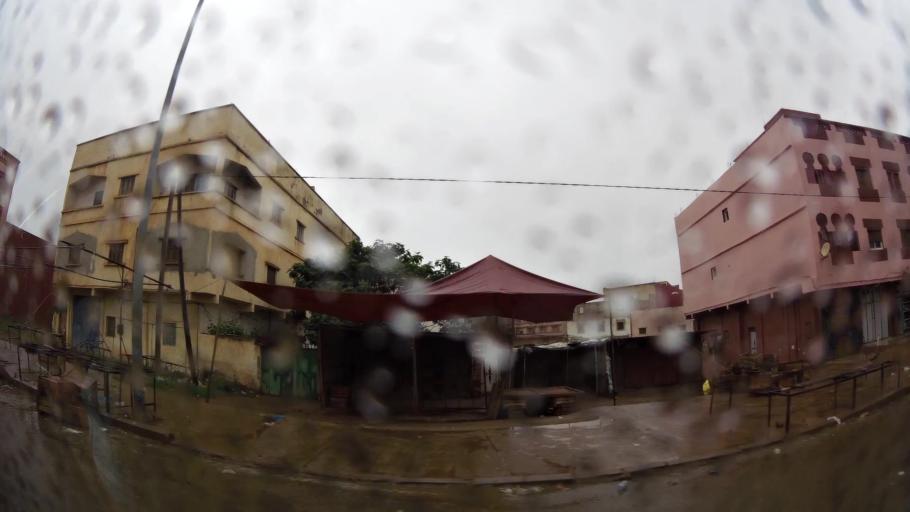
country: MA
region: Oriental
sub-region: Nador
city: Boudinar
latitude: 35.1156
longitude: -3.6416
